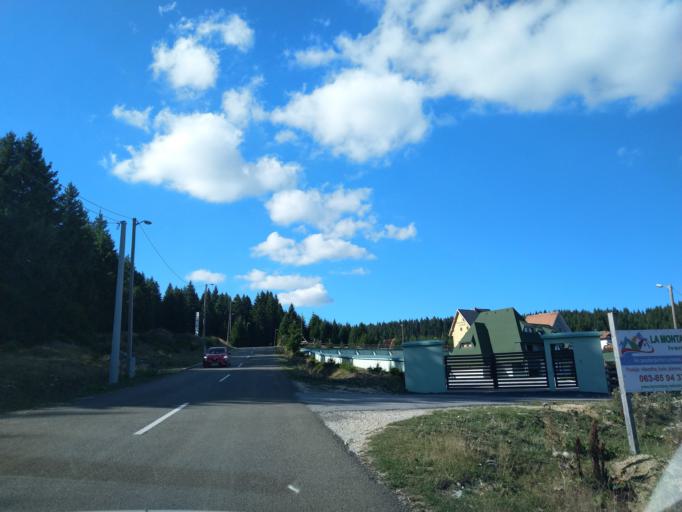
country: RS
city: Sokolovica
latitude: 43.2782
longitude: 20.3385
